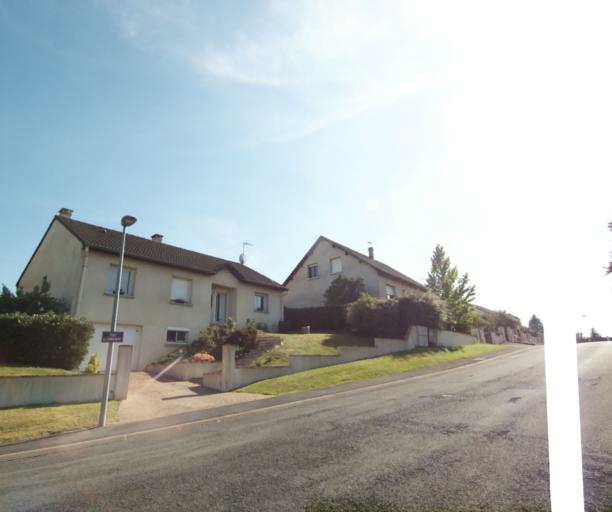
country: FR
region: Champagne-Ardenne
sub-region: Departement des Ardennes
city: Warcq
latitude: 49.7830
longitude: 4.6942
